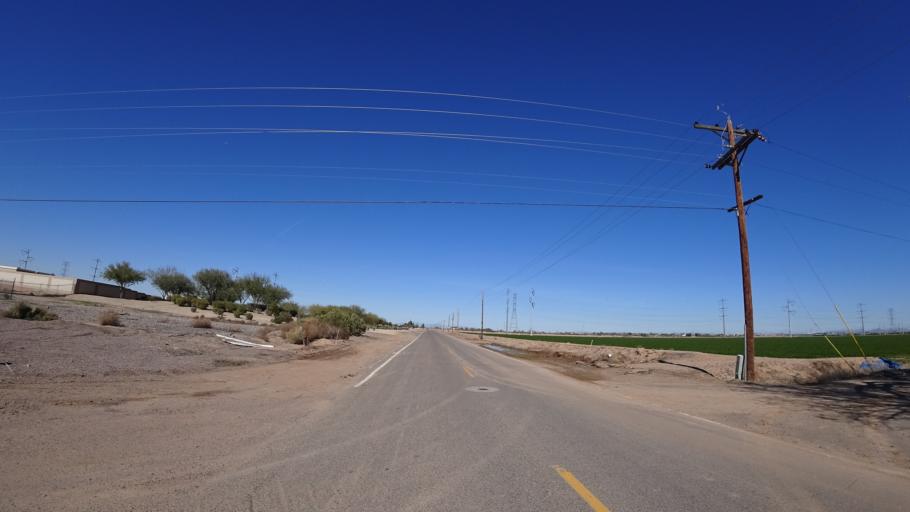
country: US
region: Arizona
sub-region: Maricopa County
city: Avondale
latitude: 33.3988
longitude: -112.3405
